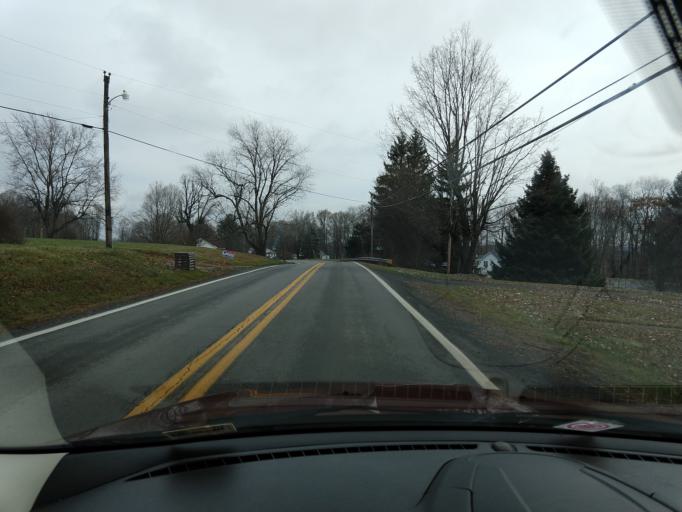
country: US
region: West Virginia
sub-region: Nicholas County
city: Craigsville
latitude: 38.2006
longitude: -80.6875
